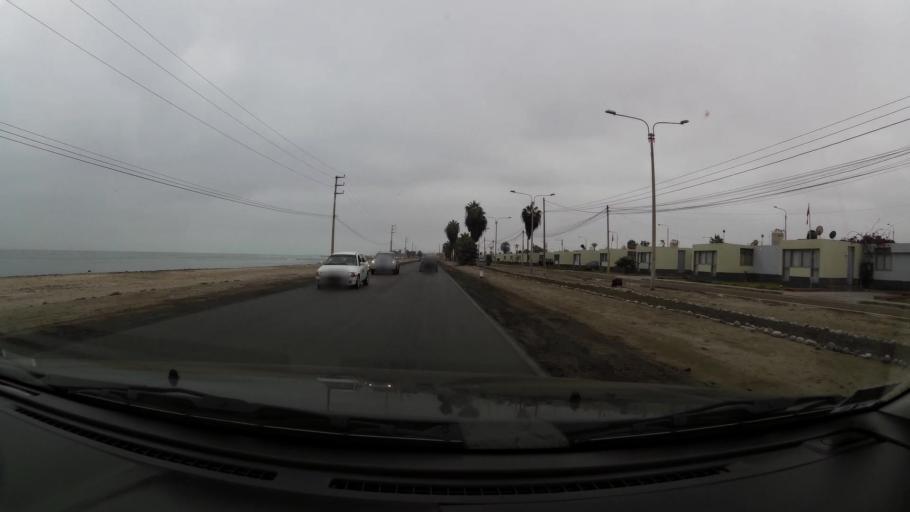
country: PE
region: Ica
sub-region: Provincia de Pisco
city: Pisco
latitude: -13.7446
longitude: -76.2277
